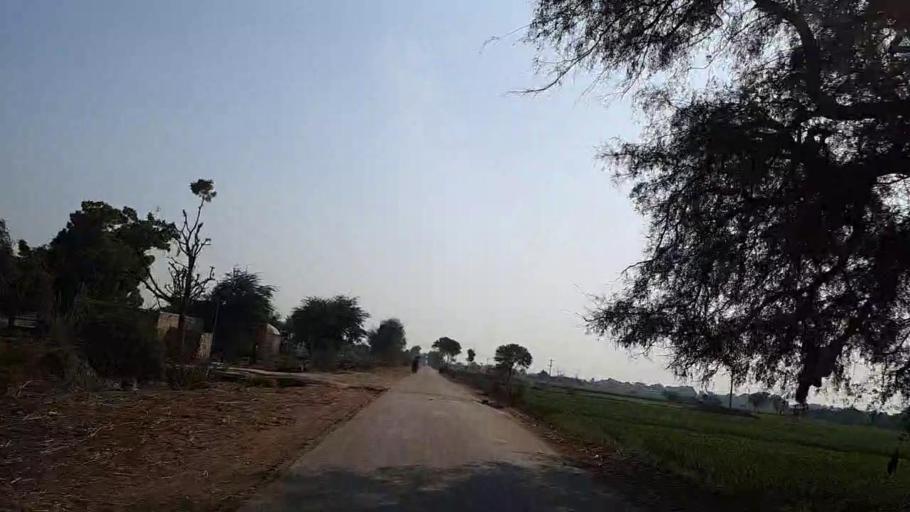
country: PK
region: Sindh
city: Sakrand
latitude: 26.0801
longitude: 68.2900
